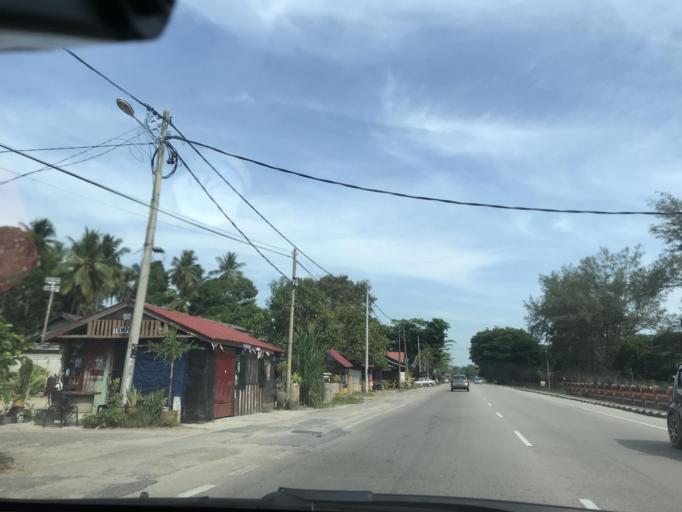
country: MY
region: Kelantan
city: Tumpat
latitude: 6.1901
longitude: 102.1561
